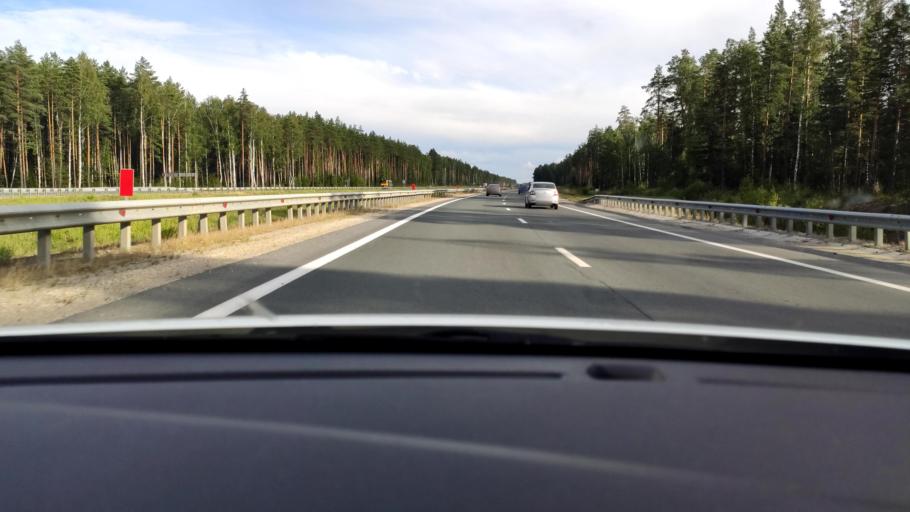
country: RU
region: Mariy-El
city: Surok
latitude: 56.5308
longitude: 48.0019
